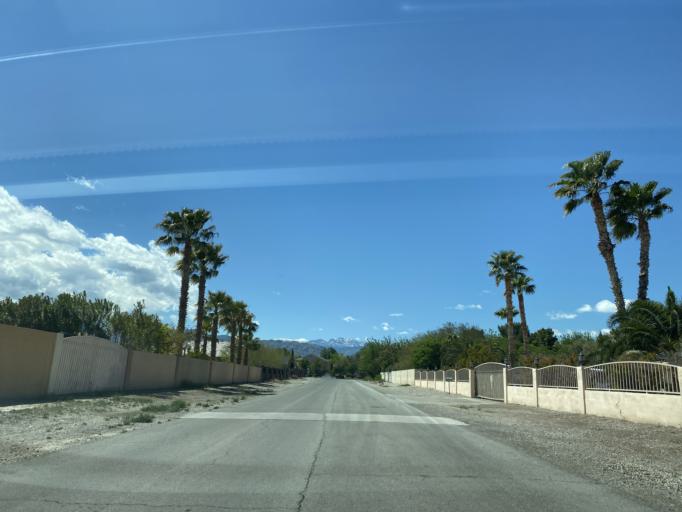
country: US
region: Nevada
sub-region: Clark County
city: North Las Vegas
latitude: 36.2997
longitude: -115.2493
